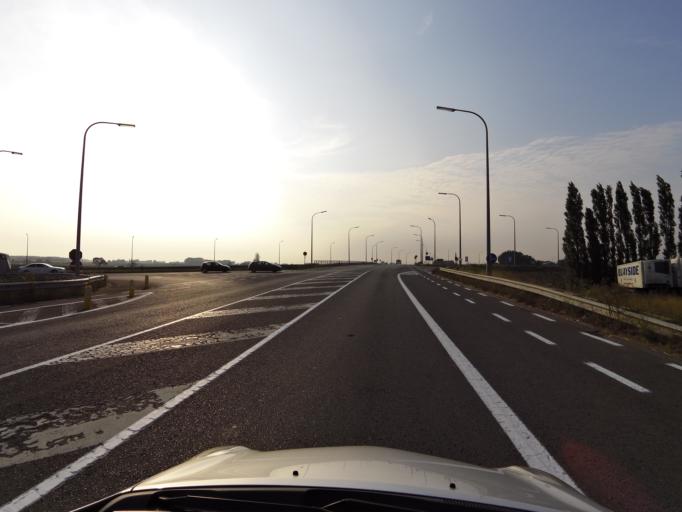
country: BE
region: Flanders
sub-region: Provincie West-Vlaanderen
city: Lichtervelde
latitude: 51.0085
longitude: 3.1729
